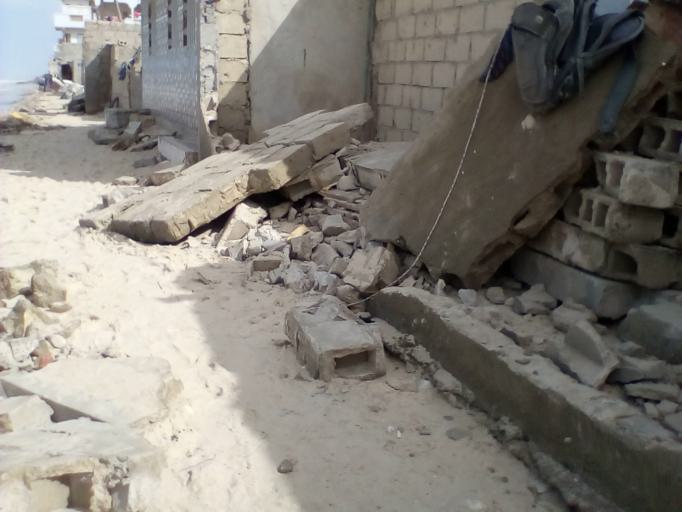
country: SN
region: Saint-Louis
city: Saint-Louis
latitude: 16.0322
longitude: -16.5090
